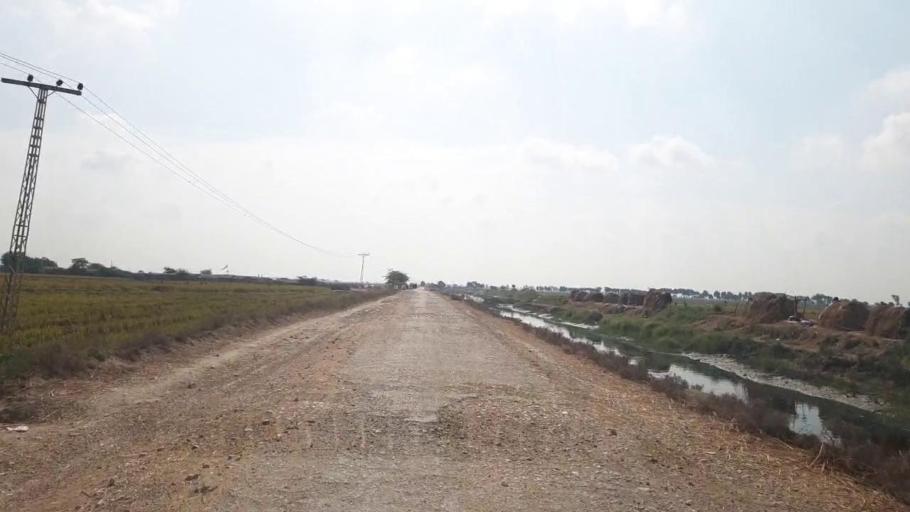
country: PK
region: Sindh
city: Kario
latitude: 24.6301
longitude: 68.5512
